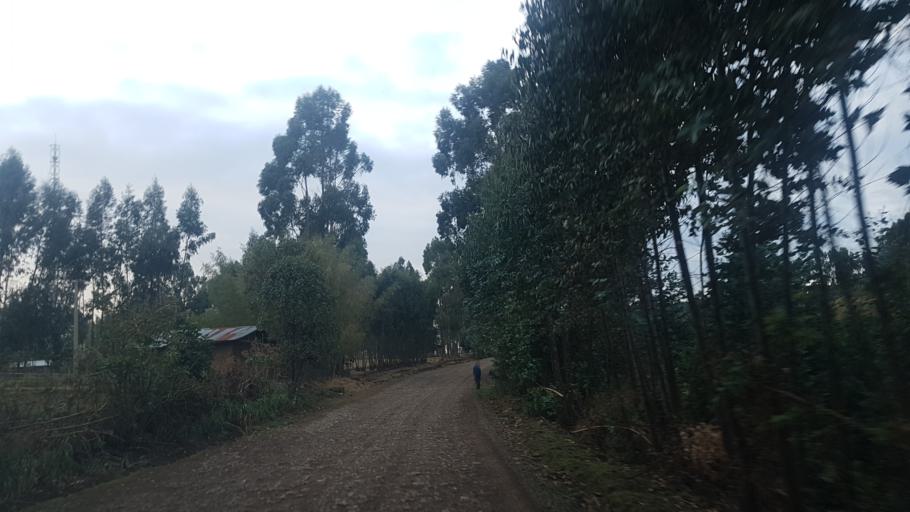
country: ET
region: Amhara
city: Finote Selam
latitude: 10.8116
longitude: 37.6520
